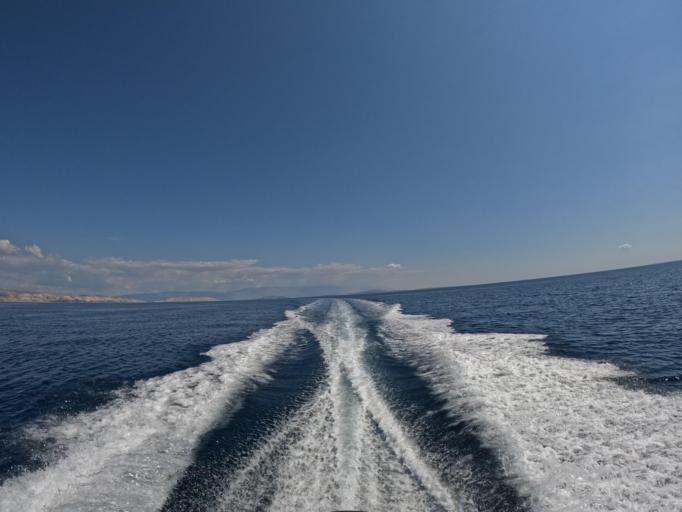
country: HR
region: Primorsko-Goranska
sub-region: Grad Krk
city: Krk
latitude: 44.9313
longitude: 14.5213
